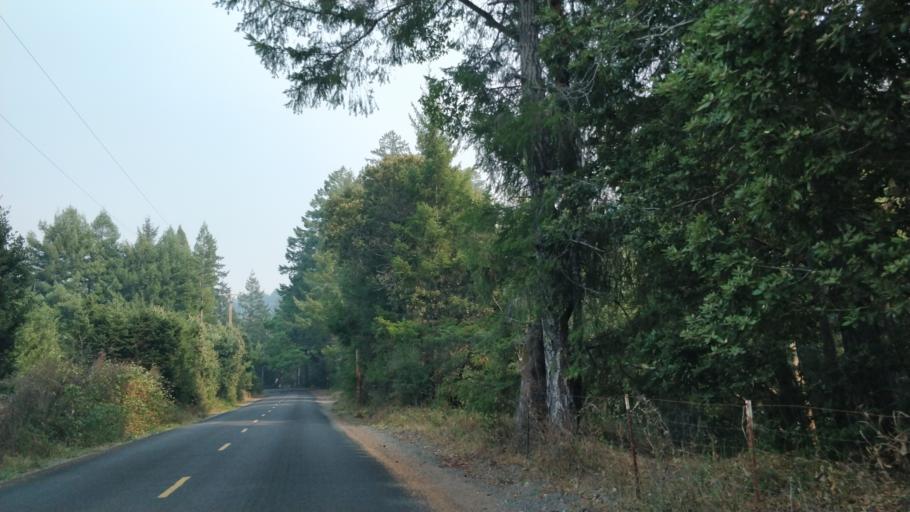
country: US
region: California
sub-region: Humboldt County
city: Rio Dell
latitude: 40.2690
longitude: -124.2252
